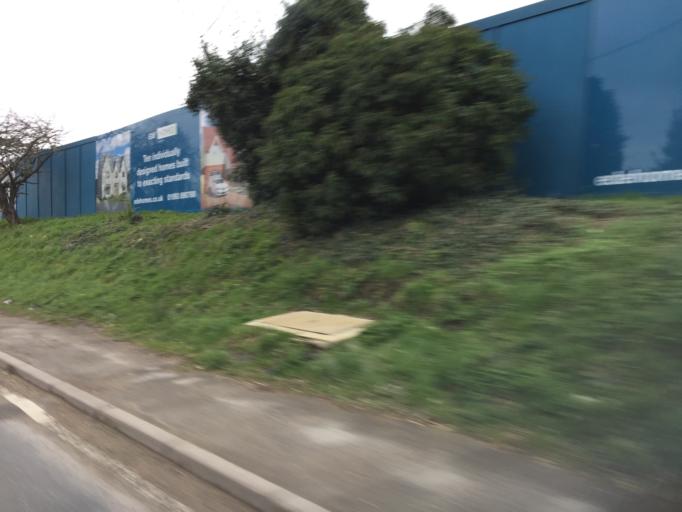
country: GB
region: England
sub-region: Oxfordshire
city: Harwell
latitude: 51.5956
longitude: -1.2957
